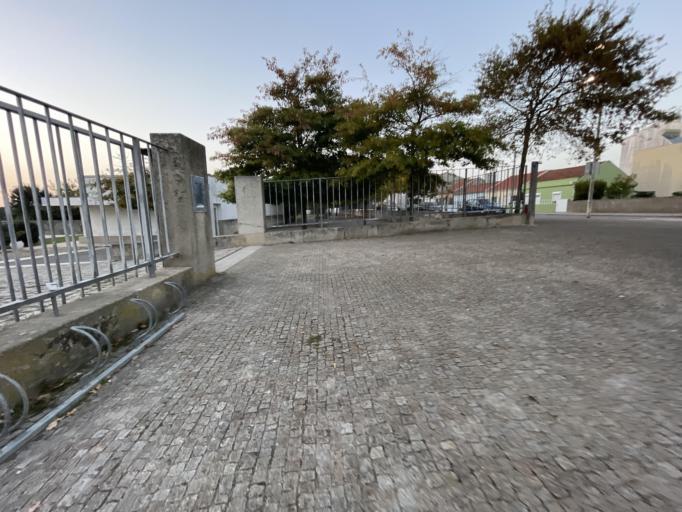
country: PT
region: Porto
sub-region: Vila do Conde
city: Vila do Conde
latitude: 41.3622
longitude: -8.7495
